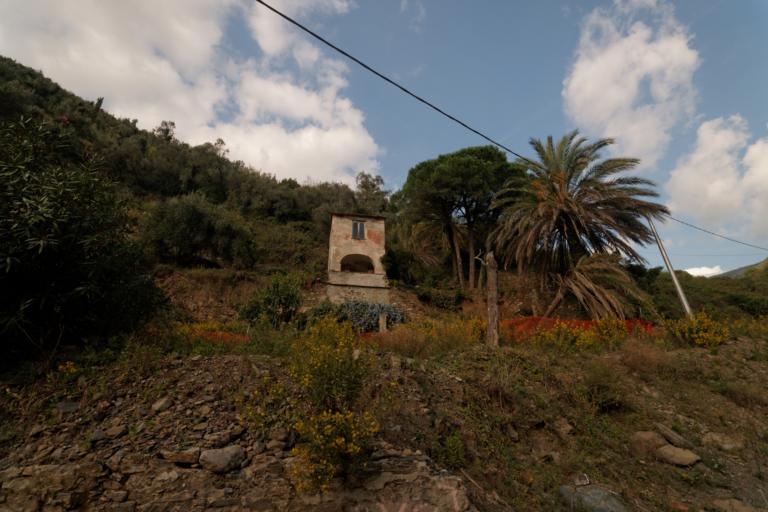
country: IT
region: Liguria
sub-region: Provincia di La Spezia
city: Vernazza
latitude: 44.1367
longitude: 9.6856
